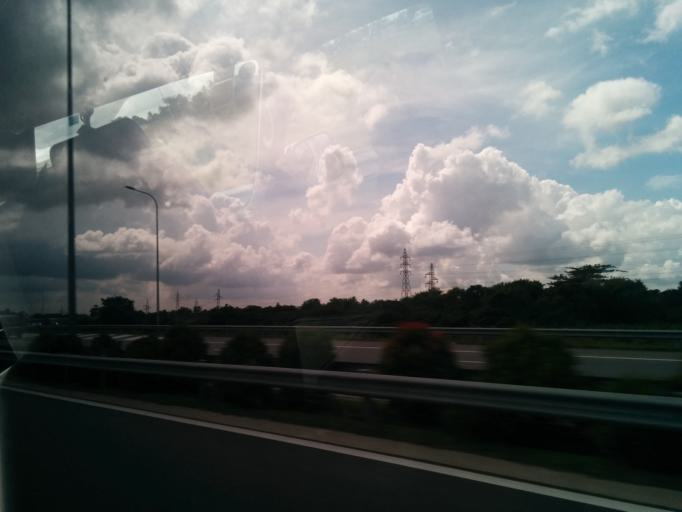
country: LK
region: Western
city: Peliyagoda
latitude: 6.9659
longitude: 79.8918
